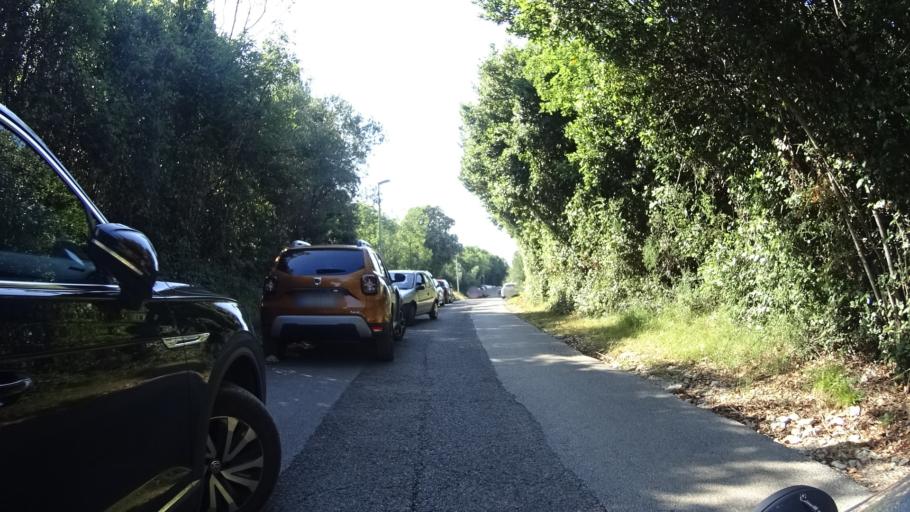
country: HR
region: Istarska
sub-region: Grad Labin
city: Rabac
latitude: 44.9971
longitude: 14.1663
